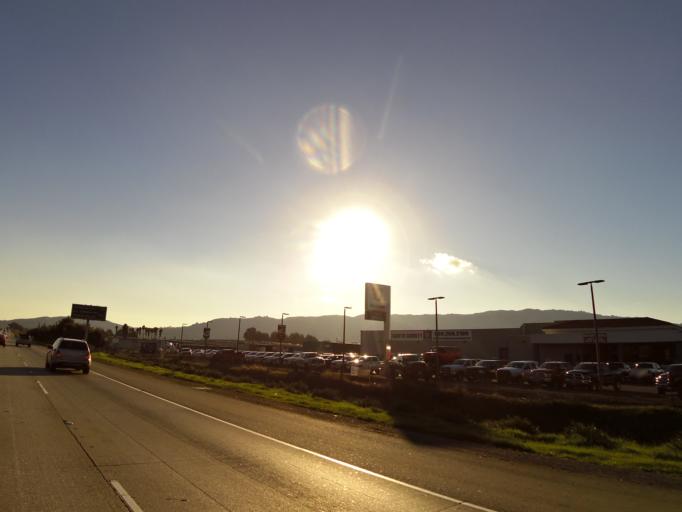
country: US
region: California
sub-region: Santa Clara County
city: Gilroy
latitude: 36.9971
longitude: -121.5566
